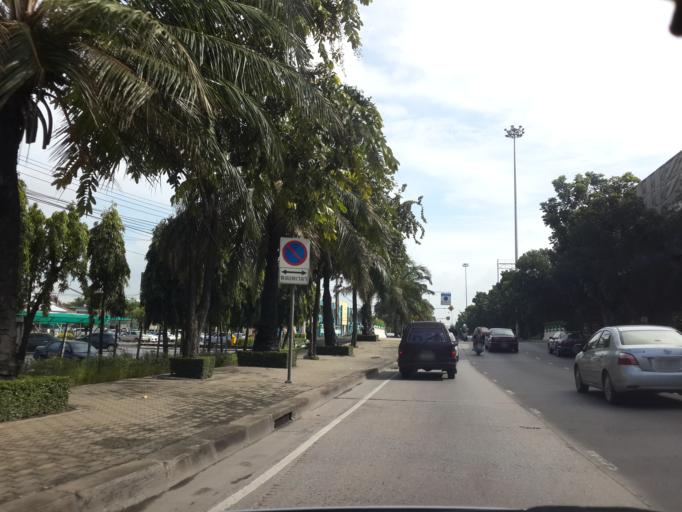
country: TH
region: Bangkok
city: Huai Khwang
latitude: 13.7633
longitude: 100.5988
